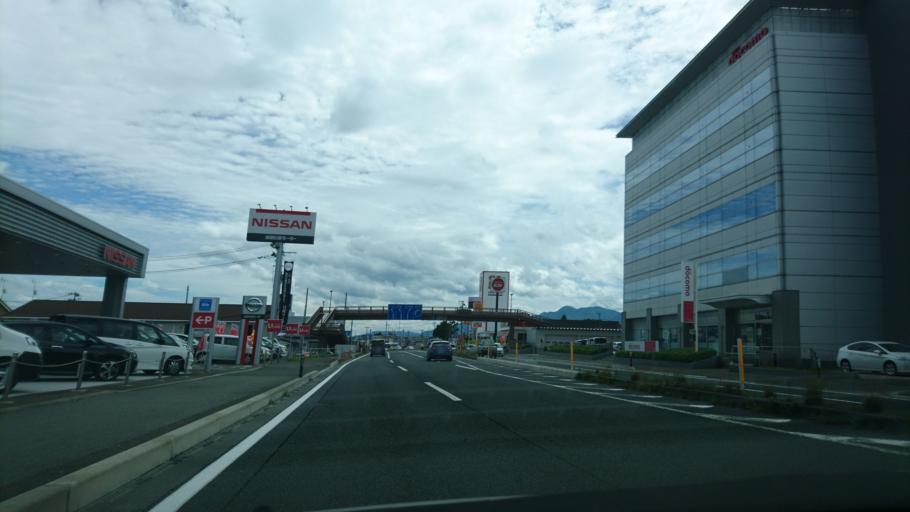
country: JP
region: Iwate
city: Morioka-shi
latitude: 39.7300
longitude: 141.1231
